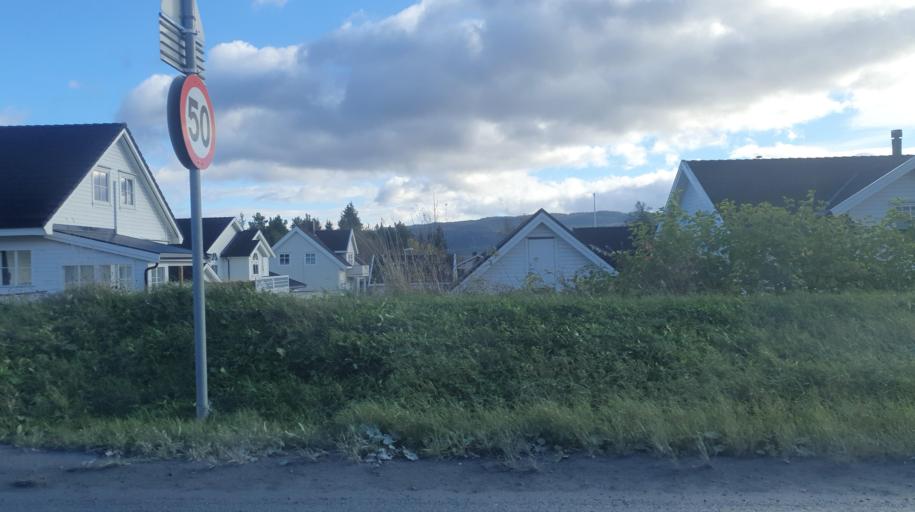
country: NO
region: Sor-Trondelag
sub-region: Klaebu
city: Klaebu
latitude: 63.3113
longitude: 10.4304
